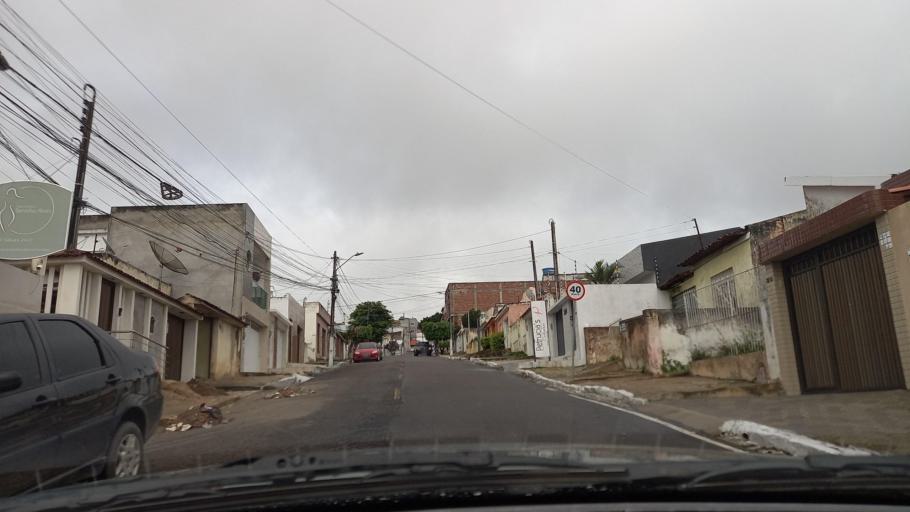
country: BR
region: Pernambuco
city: Garanhuns
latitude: -8.8953
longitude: -36.4924
